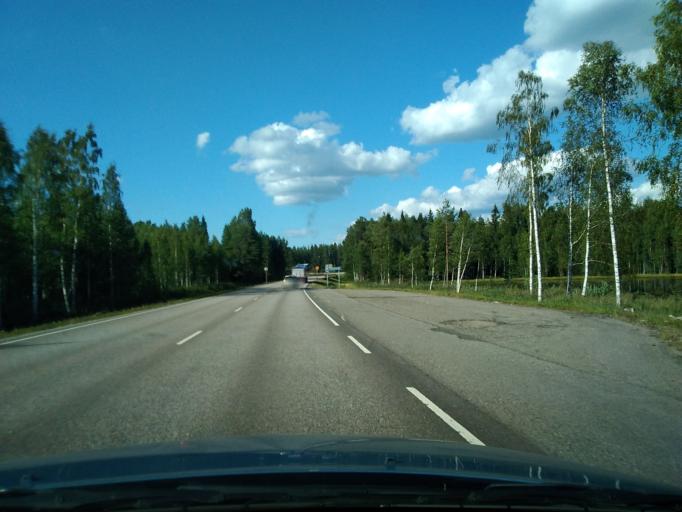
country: FI
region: Pirkanmaa
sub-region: Ylae-Pirkanmaa
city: Maenttae
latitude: 62.0939
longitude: 24.7278
